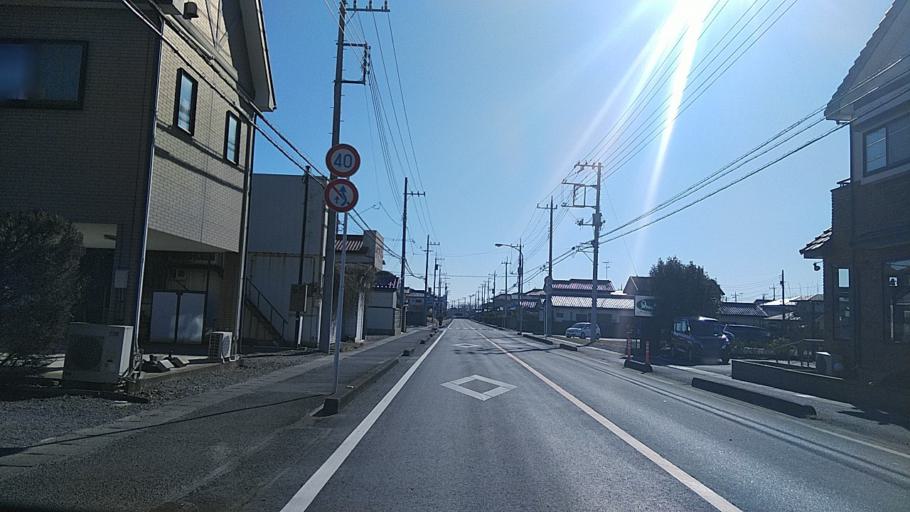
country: JP
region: Tochigi
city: Tanuma
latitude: 36.3530
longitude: 139.5569
